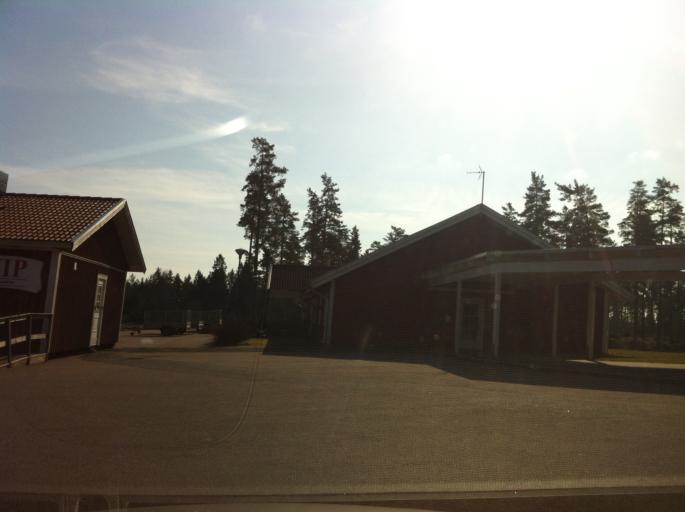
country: SE
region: Joenkoeping
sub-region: Mullsjo Kommun
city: Mullsjoe
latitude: 57.9034
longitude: 13.8624
